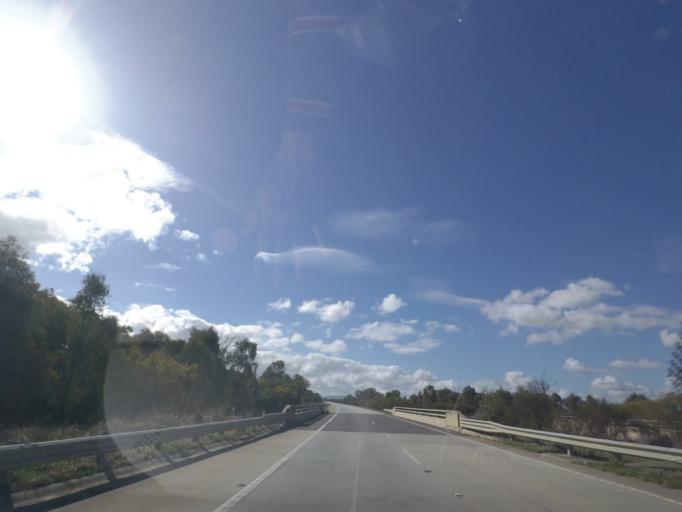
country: AU
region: New South Wales
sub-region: Albury Municipality
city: Lavington
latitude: -36.0179
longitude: 146.9843
